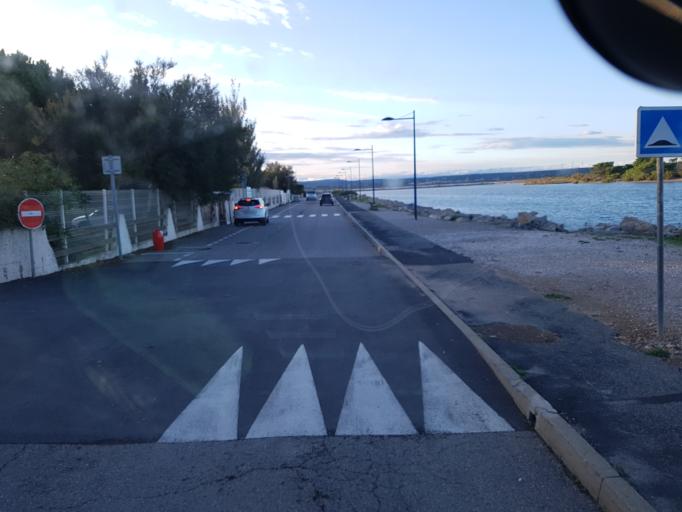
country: FR
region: Languedoc-Roussillon
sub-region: Departement de l'Aude
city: Leucate
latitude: 42.9359
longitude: 3.0311
